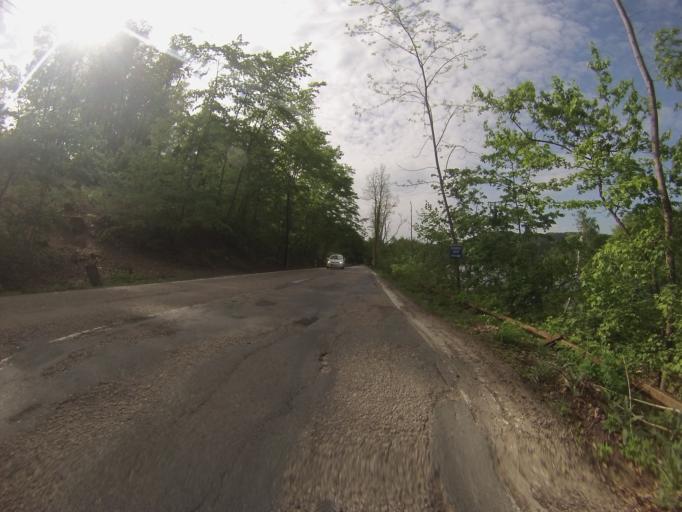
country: CZ
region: South Moravian
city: Kurim
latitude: 49.2401
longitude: 16.5028
